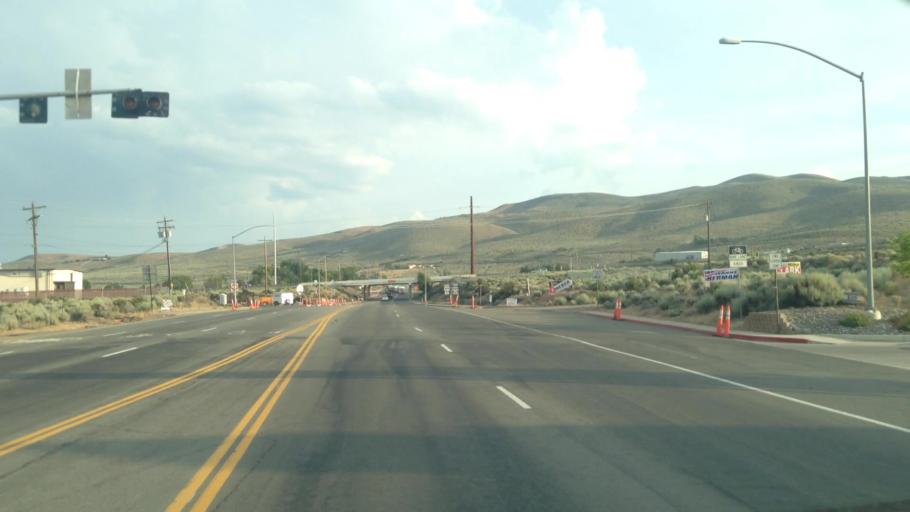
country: US
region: Nevada
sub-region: Washoe County
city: Lemmon Valley
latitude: 39.6218
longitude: -119.8822
